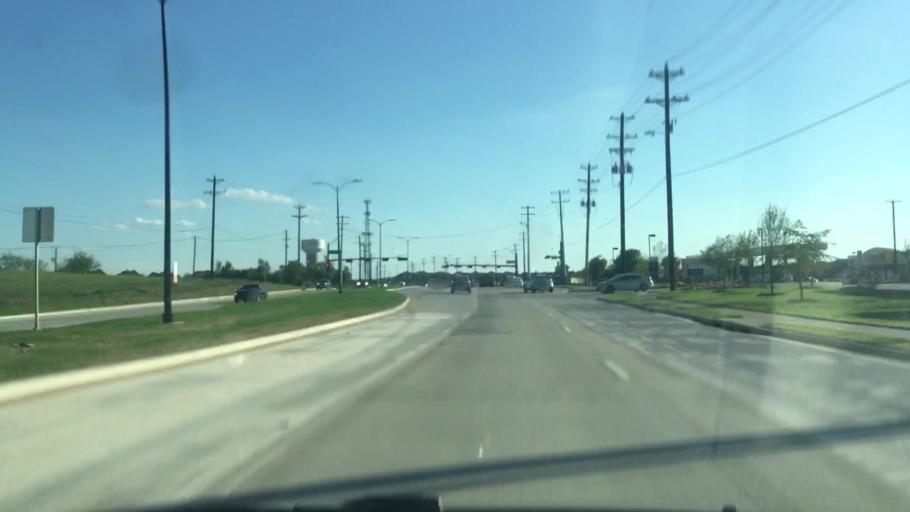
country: US
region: Texas
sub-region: Denton County
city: Little Elm
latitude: 33.1939
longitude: -96.8853
